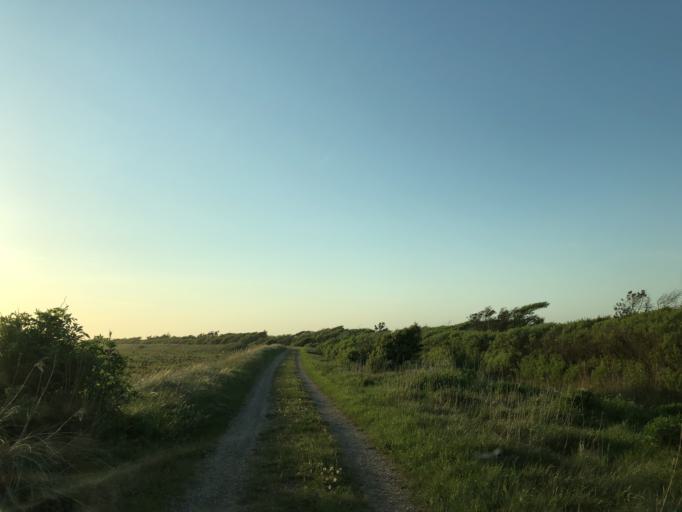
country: DK
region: Central Jutland
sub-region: Holstebro Kommune
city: Ulfborg
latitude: 56.2388
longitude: 8.1686
